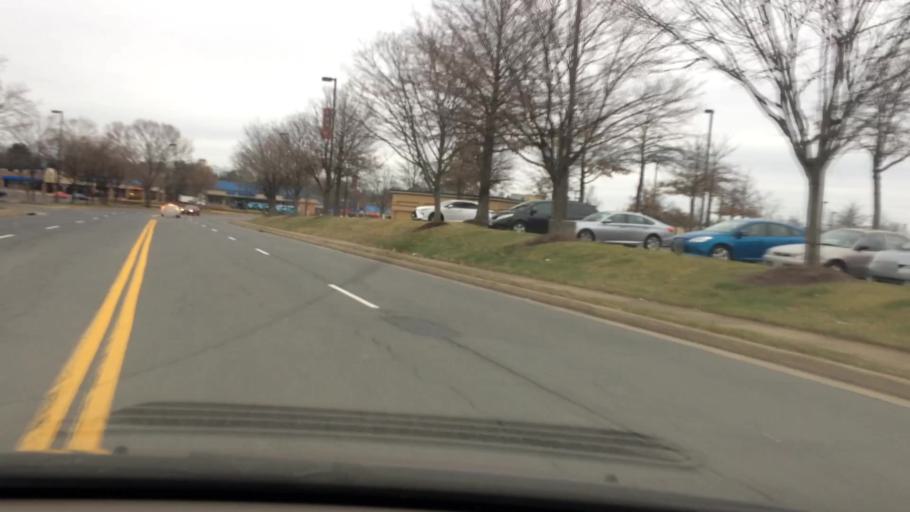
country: US
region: Virginia
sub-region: Fairfax County
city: Chantilly
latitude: 38.8959
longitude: -77.4262
